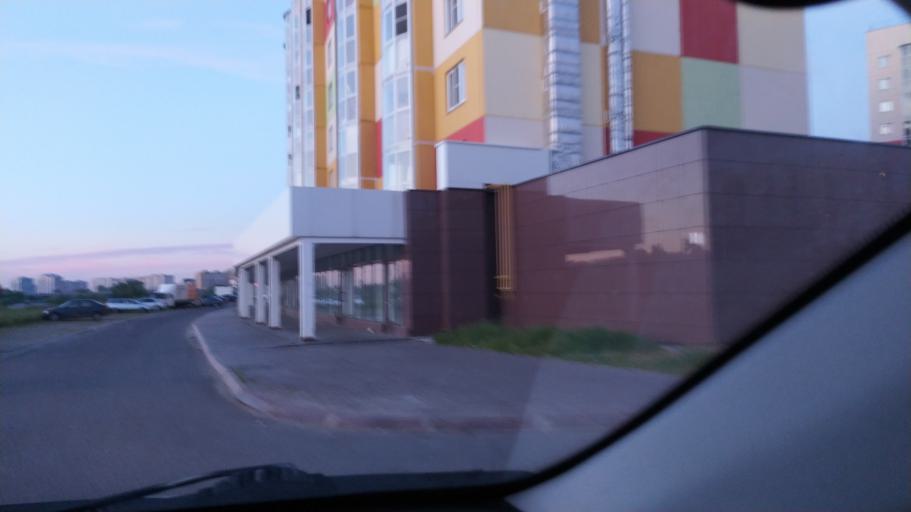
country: RU
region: Chuvashia
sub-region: Cheboksarskiy Rayon
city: Cheboksary
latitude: 56.1200
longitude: 47.2087
